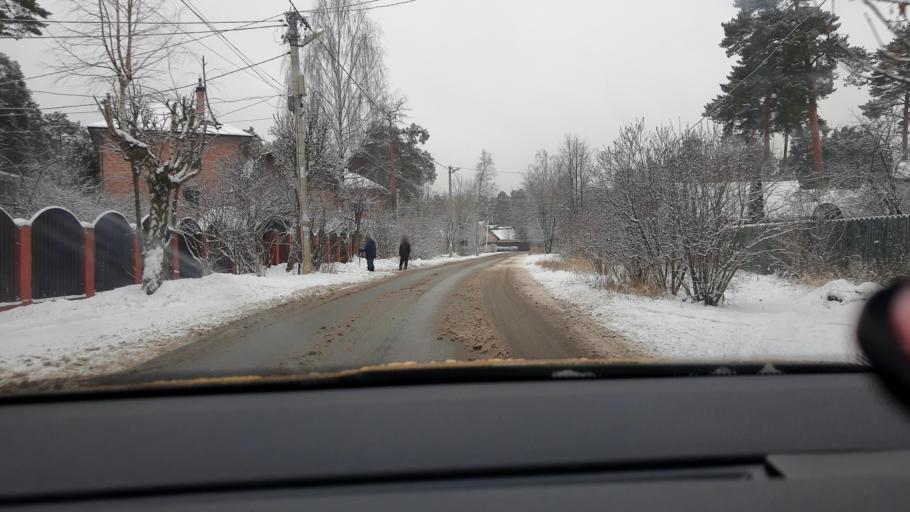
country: RU
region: Moskovskaya
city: Mamontovka
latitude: 55.9824
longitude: 37.8265
